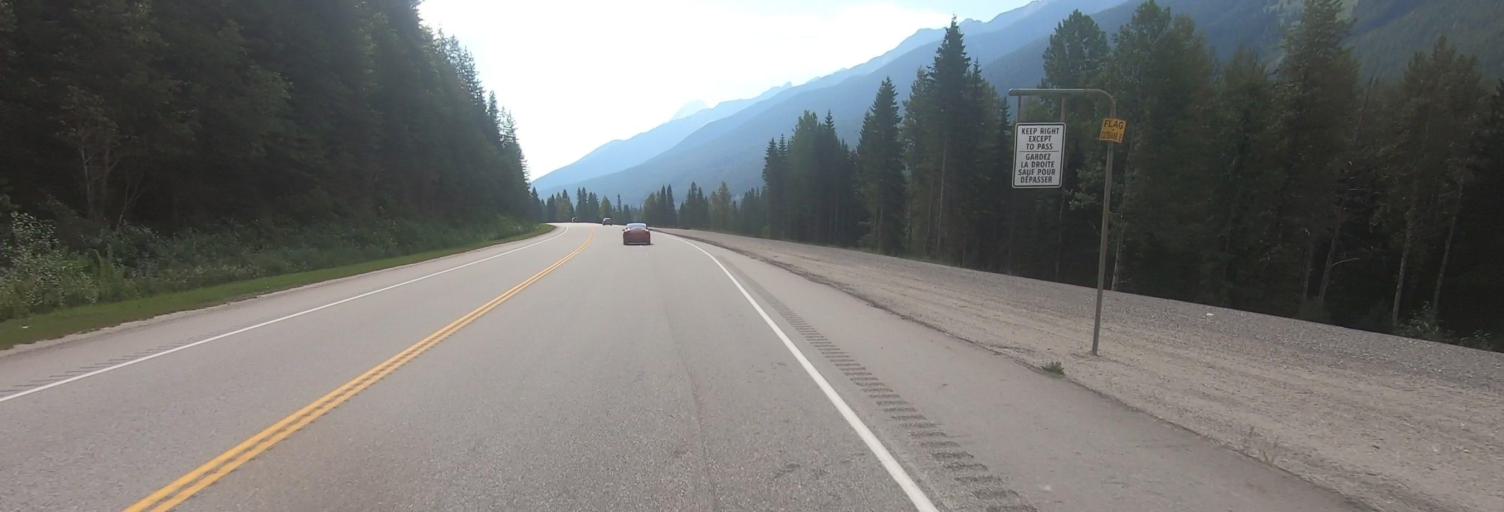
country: CA
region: British Columbia
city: Golden
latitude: 51.4090
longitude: -117.4712
